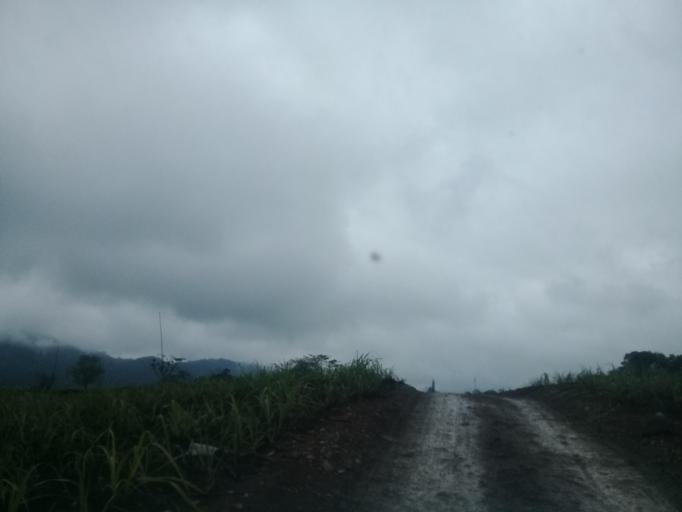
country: MX
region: Veracruz
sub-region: Amatlan de los Reyes
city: Centro de Readaptacion Social
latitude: 18.8235
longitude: -96.9505
